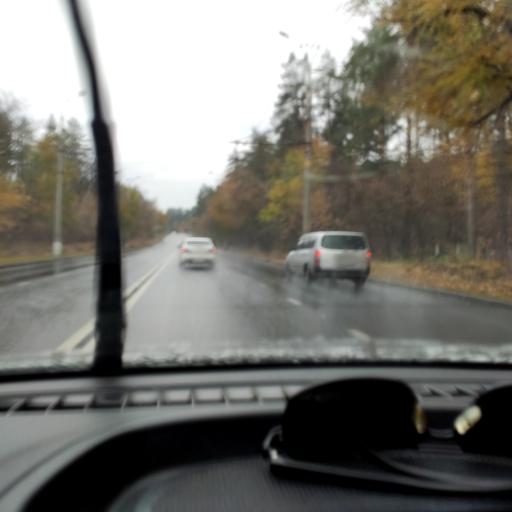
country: RU
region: Samara
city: Zhigulevsk
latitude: 53.4921
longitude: 49.4628
